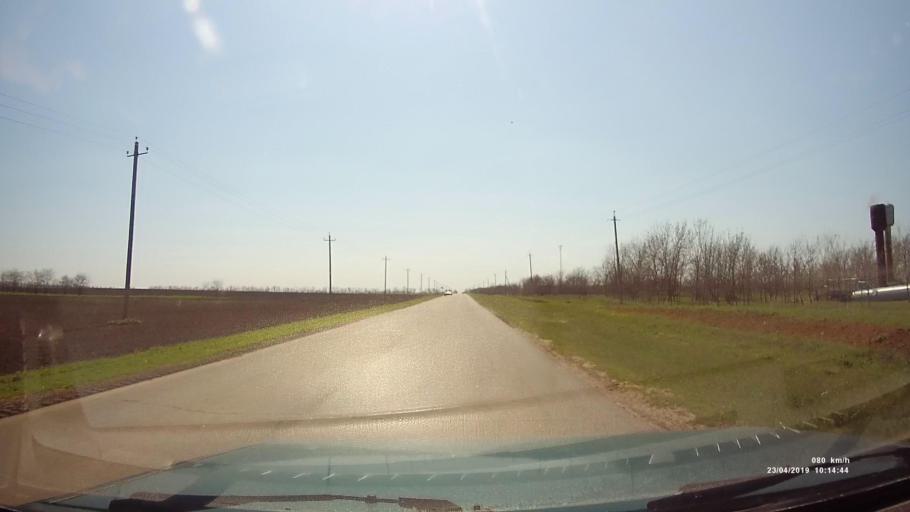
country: RU
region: Rostov
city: Sovetskoye
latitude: 46.6740
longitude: 42.3734
